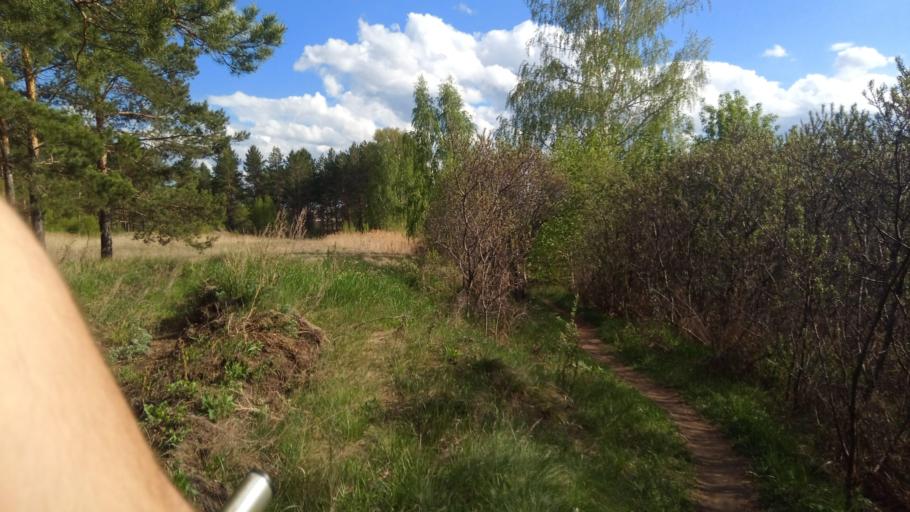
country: RU
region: Chelyabinsk
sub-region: Gorod Chelyabinsk
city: Chelyabinsk
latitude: 55.1627
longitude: 61.3126
